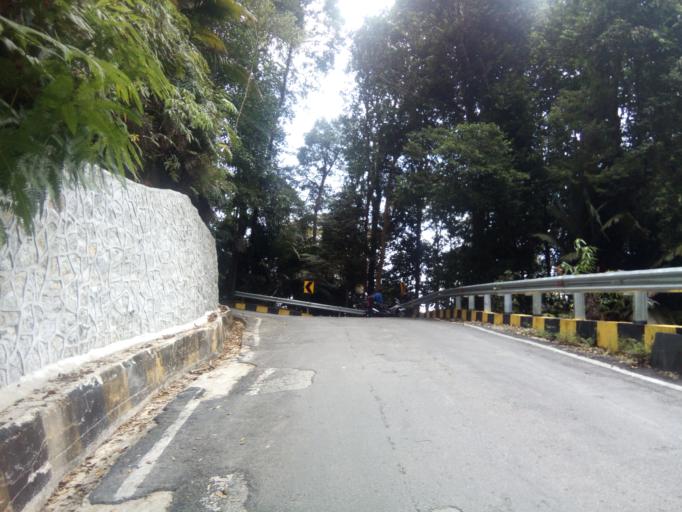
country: MY
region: Penang
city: Tanjung Tokong
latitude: 5.4267
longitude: 100.2779
